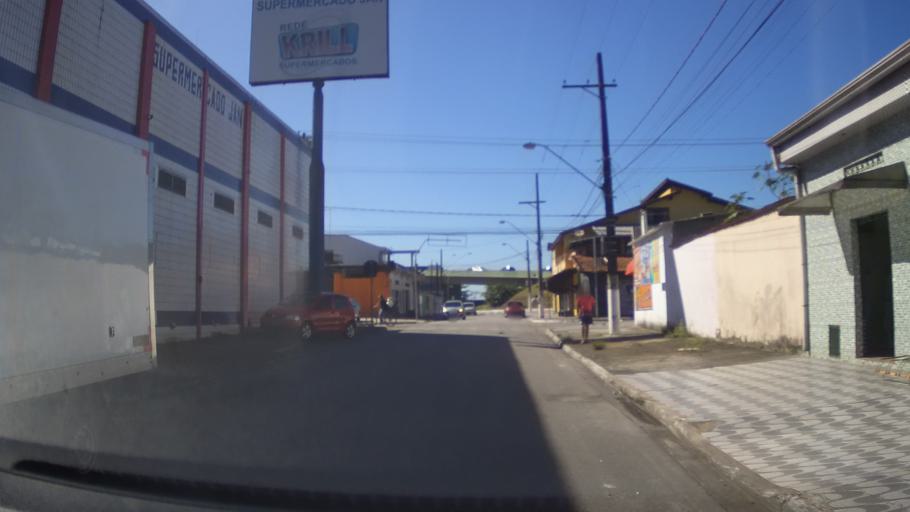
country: BR
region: Sao Paulo
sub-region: Praia Grande
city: Praia Grande
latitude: -24.0305
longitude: -46.5100
